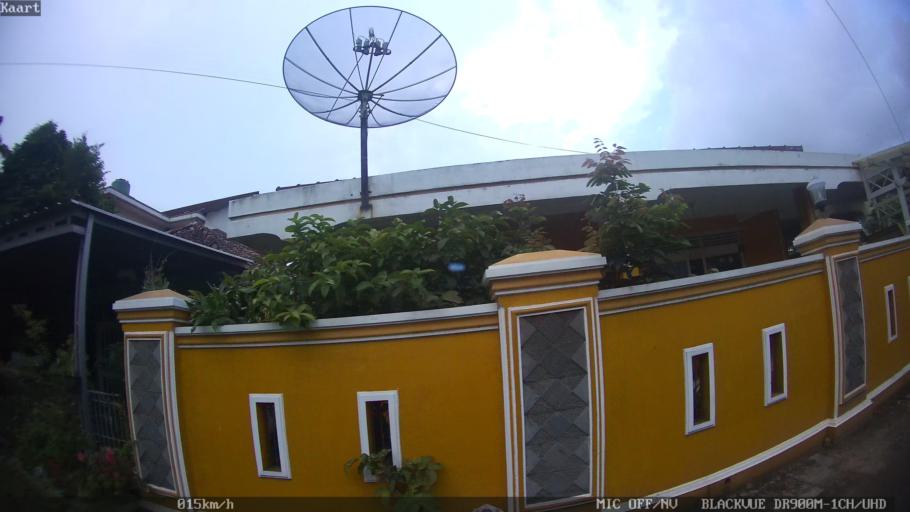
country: ID
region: Lampung
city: Bandarlampung
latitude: -5.4197
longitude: 105.2736
